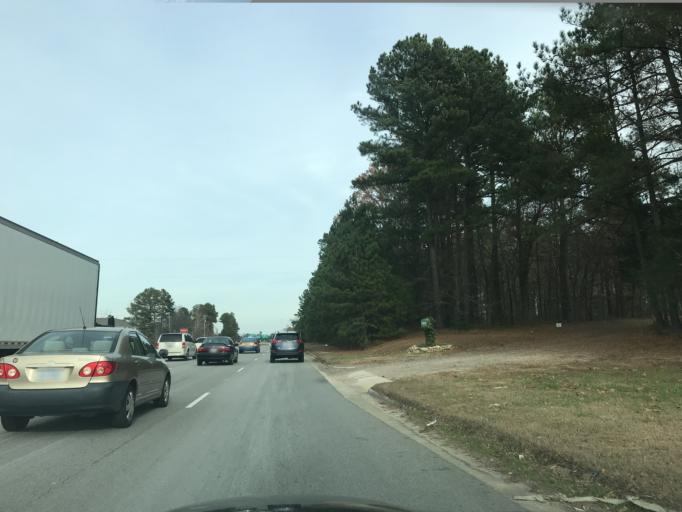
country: US
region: North Carolina
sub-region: Wake County
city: Knightdale
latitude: 35.8560
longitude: -78.5547
